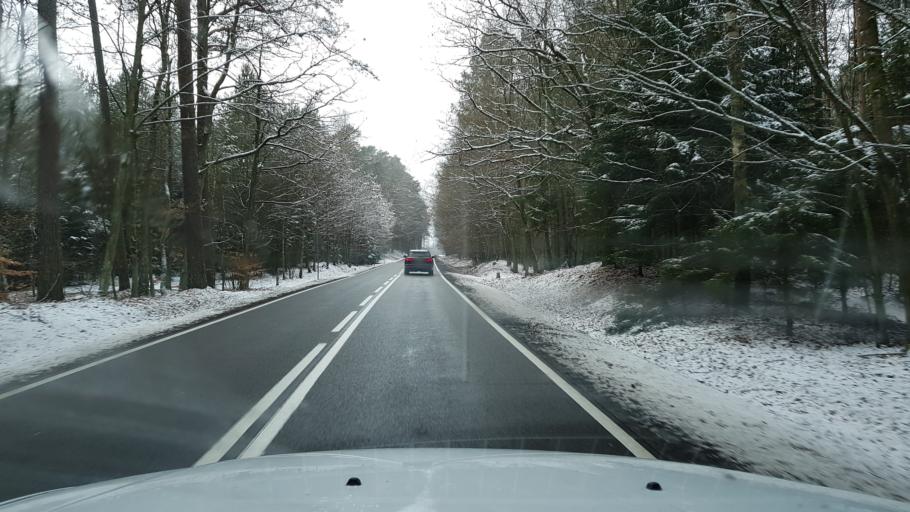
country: PL
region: West Pomeranian Voivodeship
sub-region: Powiat drawski
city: Zlocieniec
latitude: 53.5346
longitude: 16.0849
